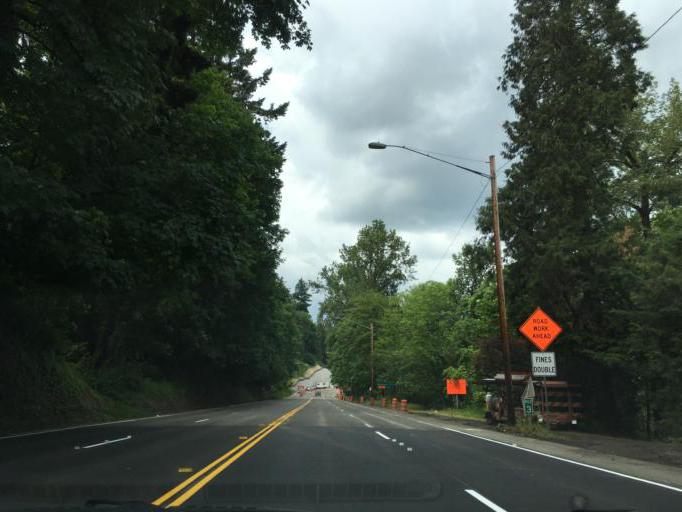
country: US
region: Oregon
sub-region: Clackamas County
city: Milwaukie
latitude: 45.4593
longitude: -122.6660
